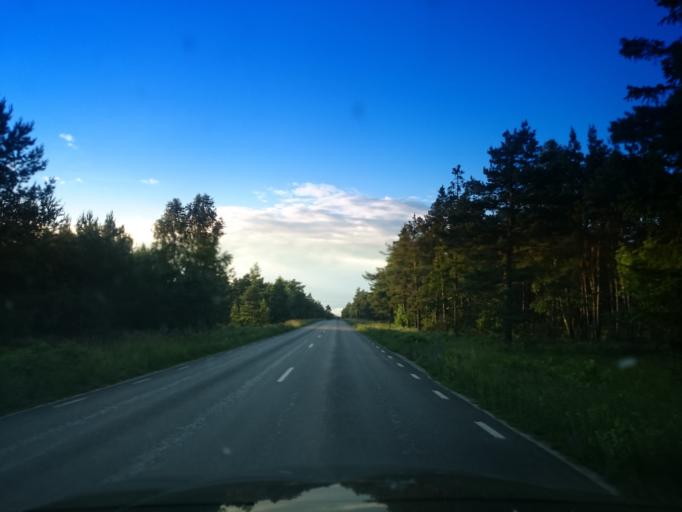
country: SE
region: Gotland
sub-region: Gotland
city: Hemse
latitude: 57.3299
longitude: 18.3802
